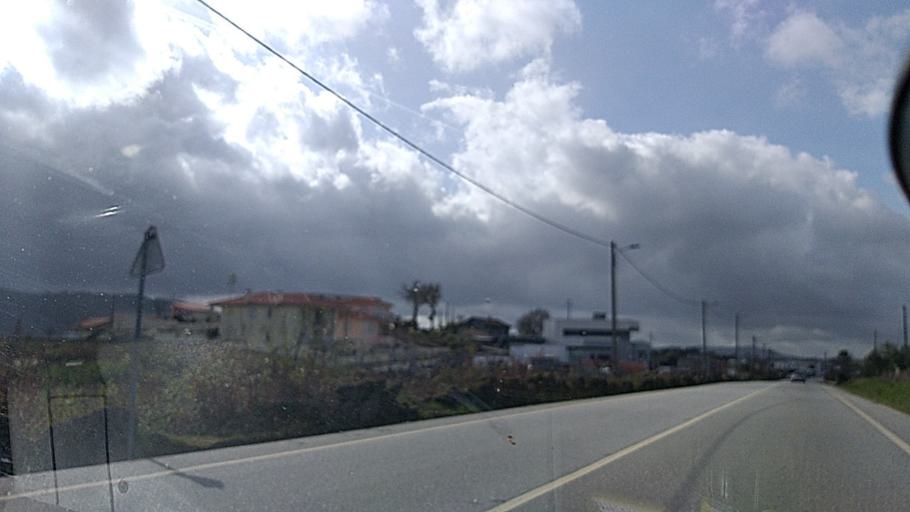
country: PT
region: Viseu
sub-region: Satao
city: Satao
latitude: 40.6688
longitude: -7.7113
